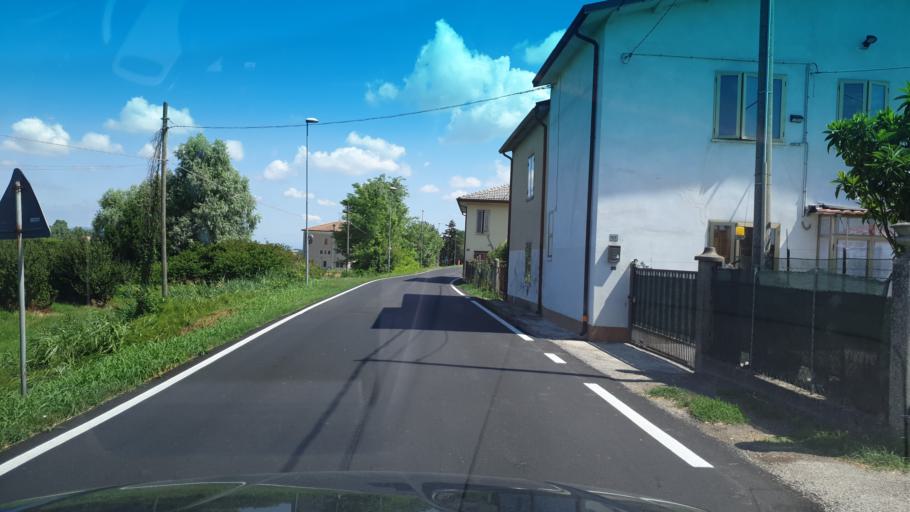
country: IT
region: Veneto
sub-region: Provincia di Rovigo
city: Costa di Rovigo
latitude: 45.0468
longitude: 11.6854
